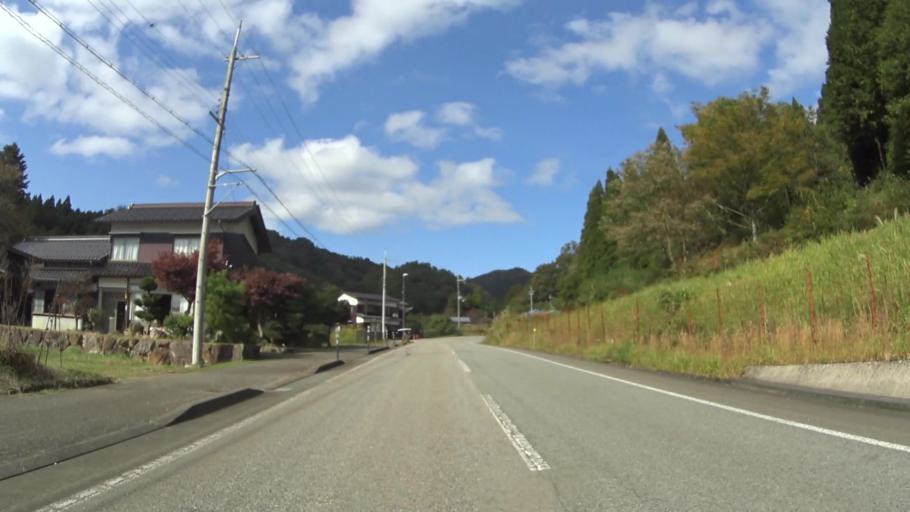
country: JP
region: Hyogo
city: Toyooka
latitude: 35.5112
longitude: 134.9920
